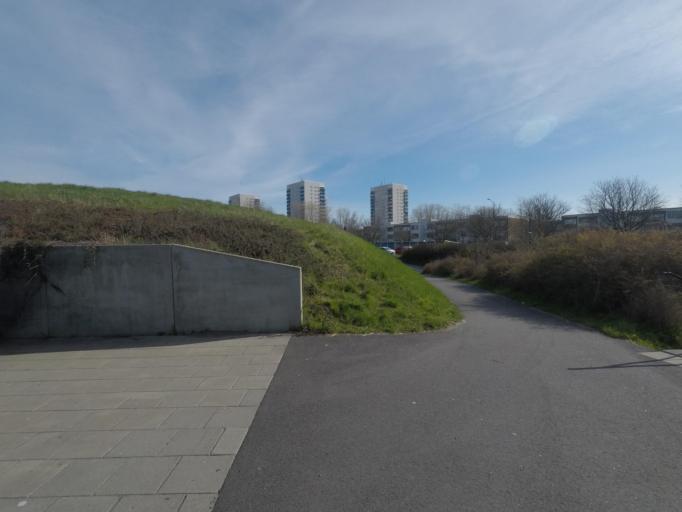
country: SE
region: Skane
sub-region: Malmo
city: Tygelsjo
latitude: 55.5576
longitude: 13.0039
